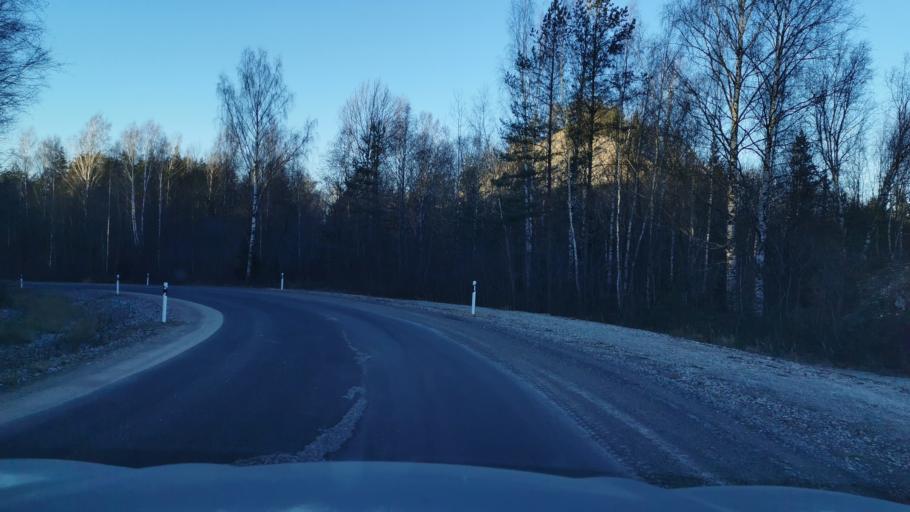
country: EE
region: Ida-Virumaa
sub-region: Kohtla-Nomme vald
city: Kohtla-Nomme
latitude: 59.3509
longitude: 27.1688
